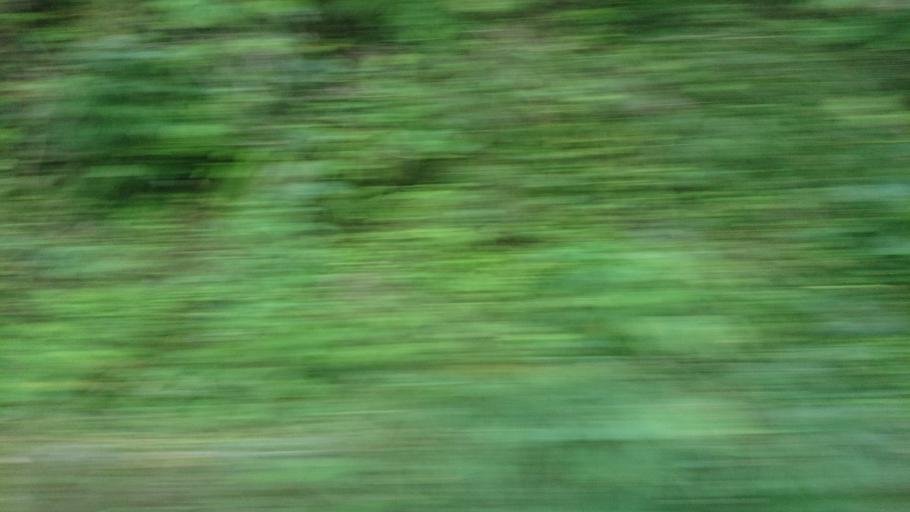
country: TW
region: Taiwan
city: Daxi
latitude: 24.8799
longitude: 121.3811
